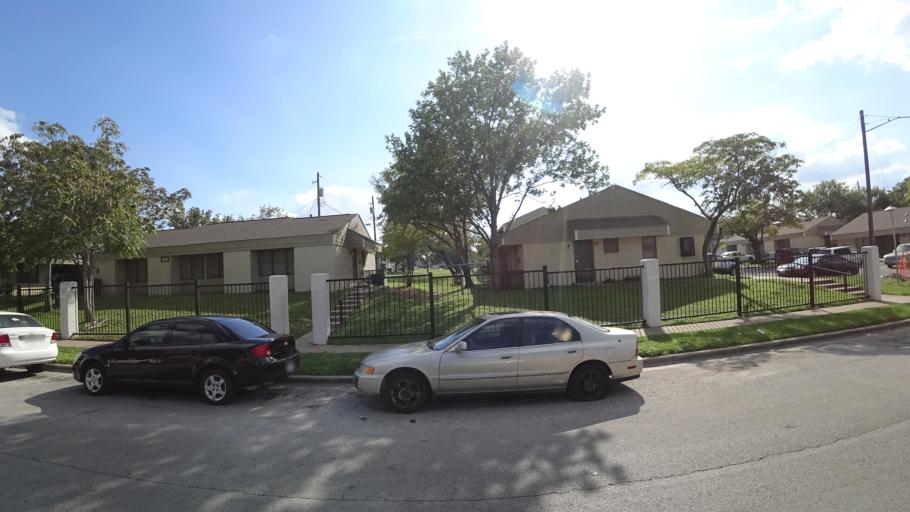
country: US
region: Texas
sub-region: Travis County
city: Austin
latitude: 30.3540
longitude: -97.7069
